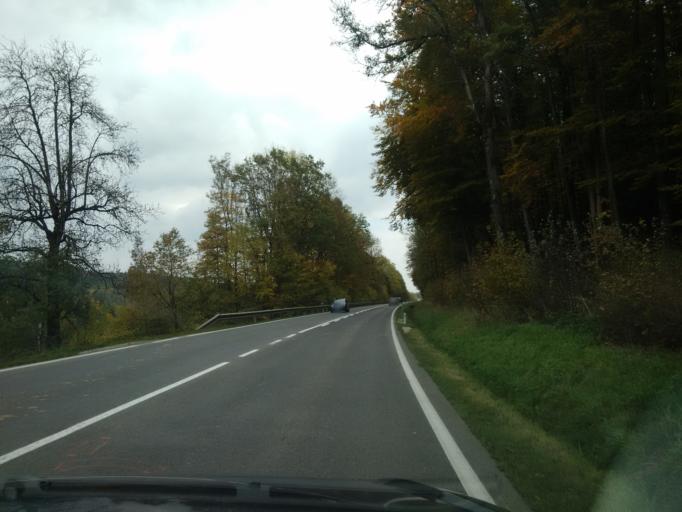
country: AT
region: Upper Austria
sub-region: Politischer Bezirk Vocklabruck
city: Attnang-Puchheim
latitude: 48.0073
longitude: 13.6936
